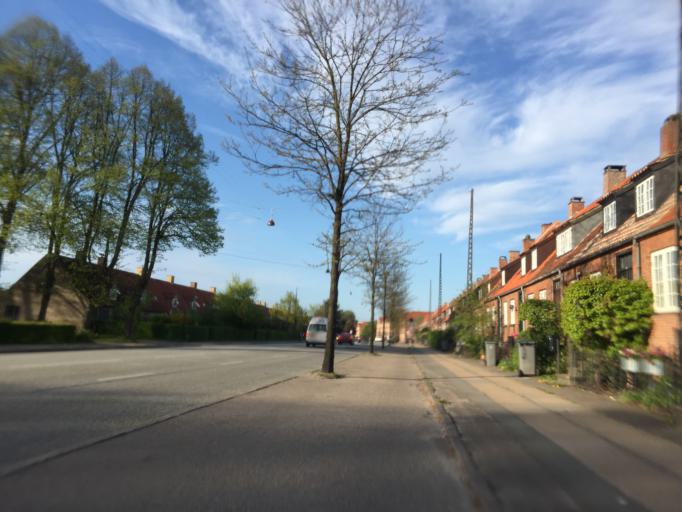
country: DK
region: Capital Region
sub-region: Frederiksberg Kommune
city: Frederiksberg
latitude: 55.6966
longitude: 12.5132
